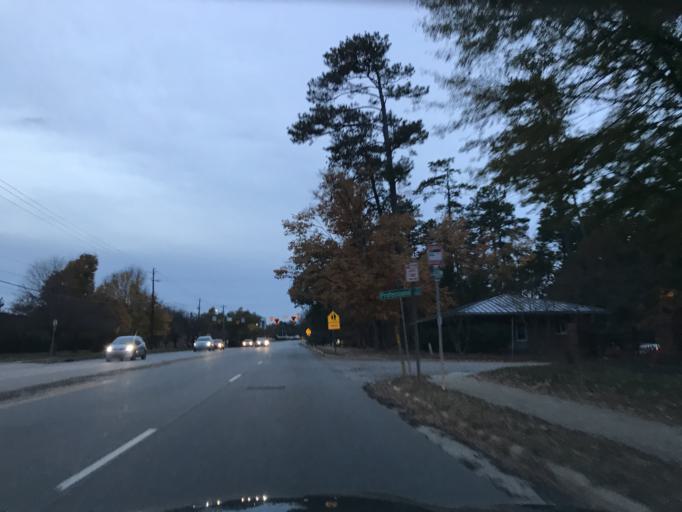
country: US
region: North Carolina
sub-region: Wake County
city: Raleigh
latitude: 35.8502
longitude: -78.6087
